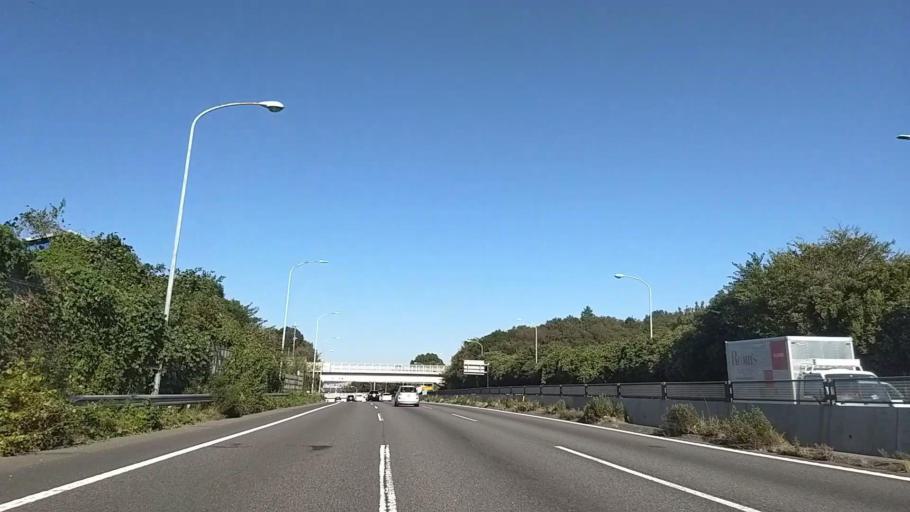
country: JP
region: Kanagawa
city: Minami-rinkan
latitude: 35.4717
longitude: 139.5319
